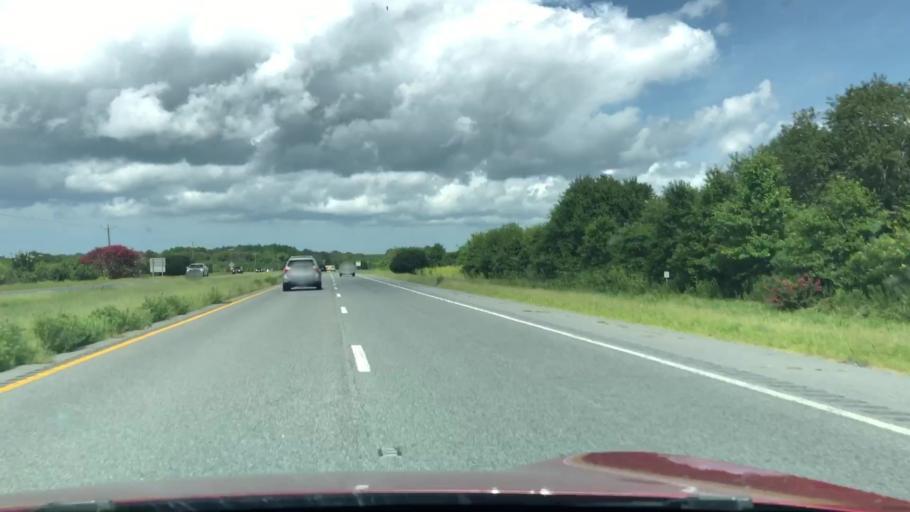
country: US
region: Virginia
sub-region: Northampton County
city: Cape Charles
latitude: 37.1424
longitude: -75.9675
